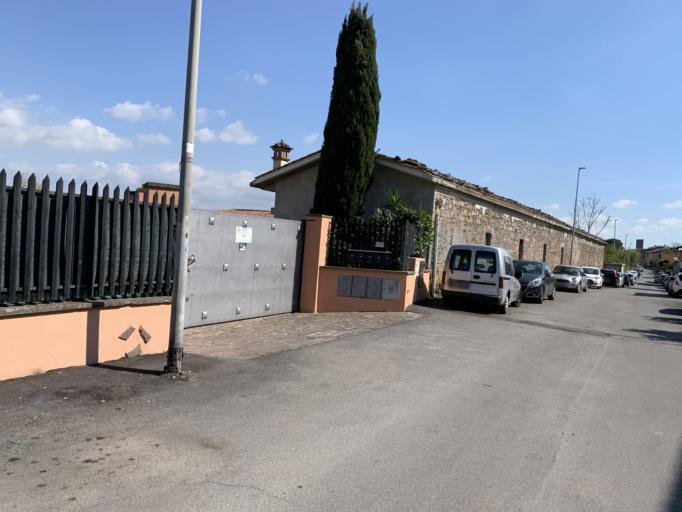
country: IT
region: Latium
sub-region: Citta metropolitana di Roma Capitale
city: Rome
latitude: 41.8624
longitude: 12.5435
